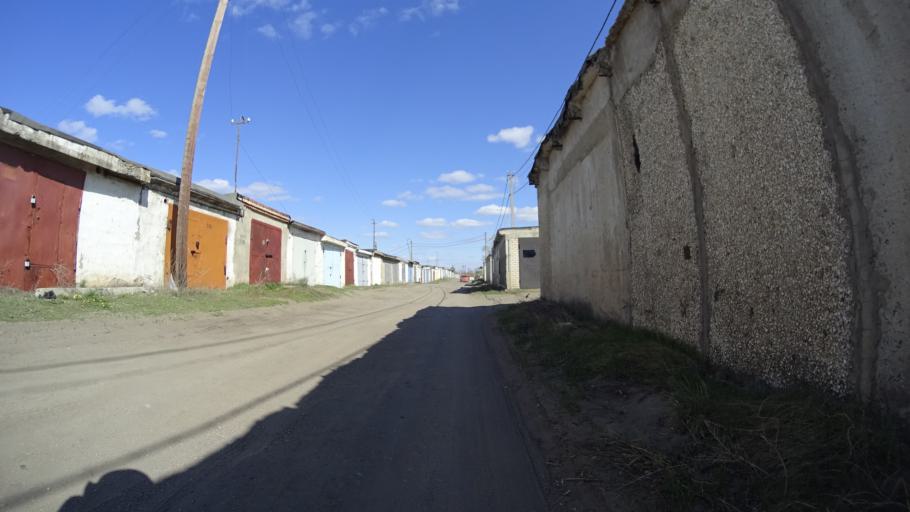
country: RU
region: Chelyabinsk
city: Troitsk
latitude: 54.0831
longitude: 61.5247
